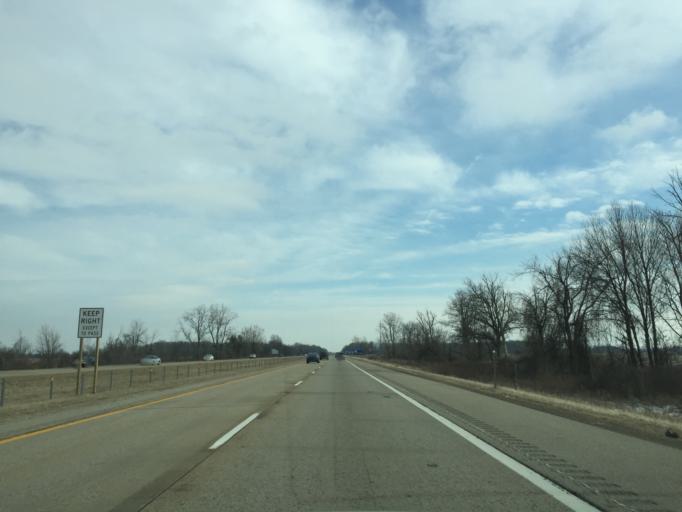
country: US
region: Michigan
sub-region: Ionia County
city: Lake Odessa
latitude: 42.8791
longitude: -85.1147
